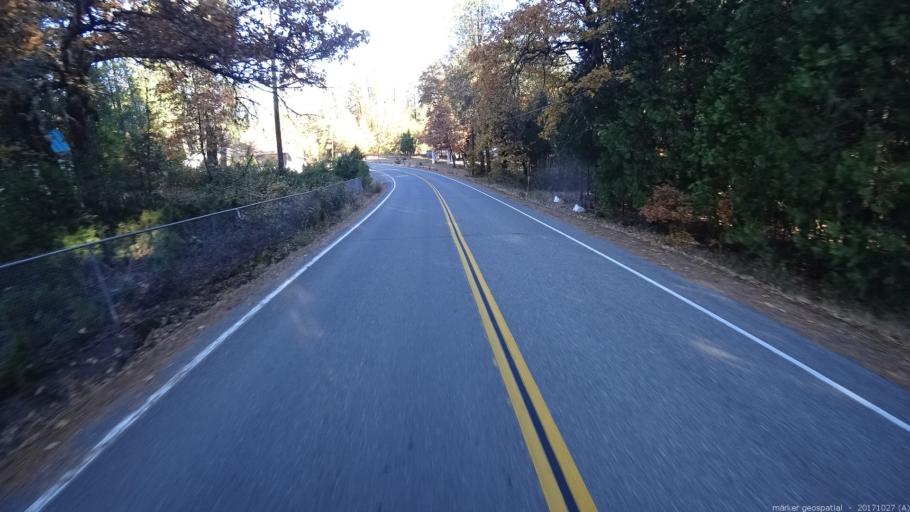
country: US
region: California
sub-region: Shasta County
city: Burney
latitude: 41.0164
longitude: -121.9070
